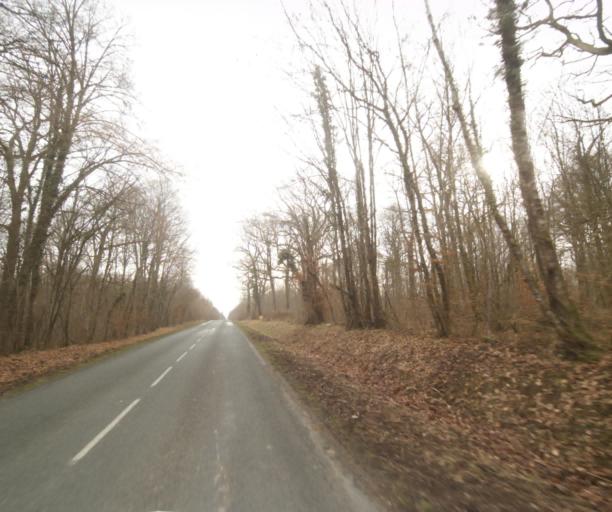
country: FR
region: Champagne-Ardenne
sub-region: Departement de la Marne
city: Pargny-sur-Saulx
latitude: 48.7262
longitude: 4.8699
